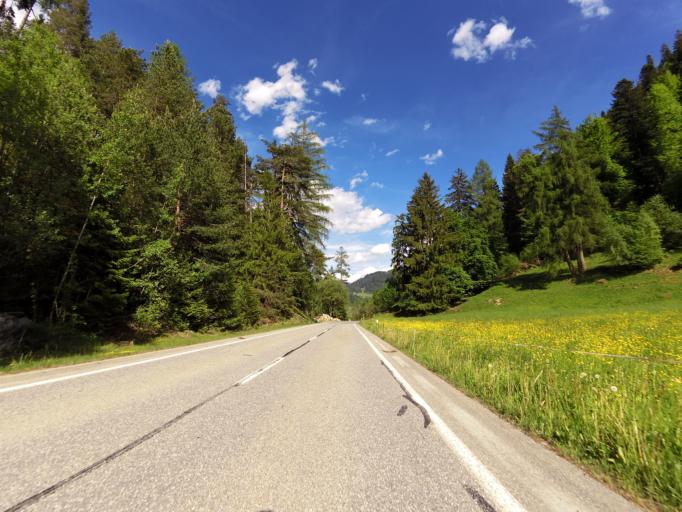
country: CH
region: Grisons
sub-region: Imboden District
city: Flims
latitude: 46.7946
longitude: 9.3183
